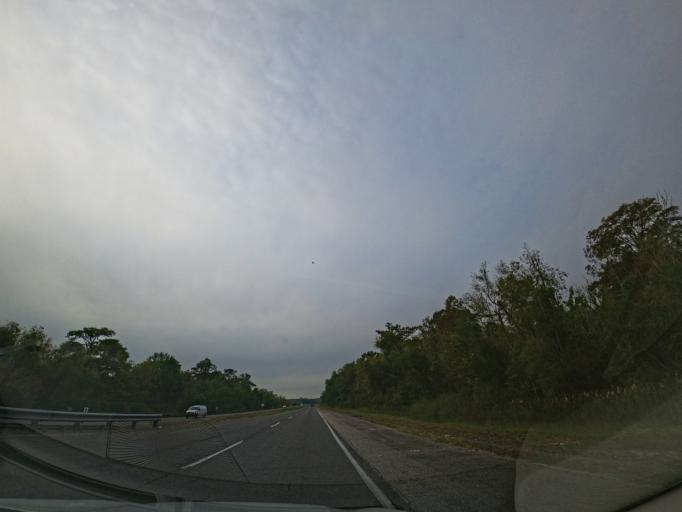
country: US
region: Louisiana
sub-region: Terrebonne Parish
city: Houma
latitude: 29.6323
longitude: -90.6623
